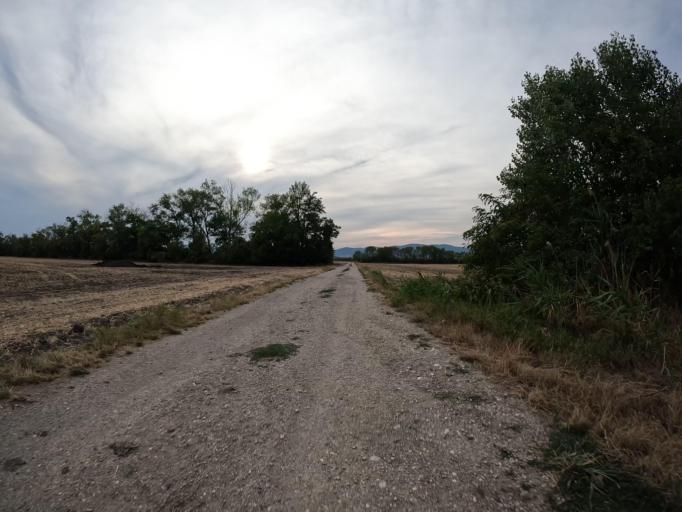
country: AT
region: Lower Austria
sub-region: Politischer Bezirk Baden
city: Trumau
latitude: 48.0037
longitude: 16.3343
